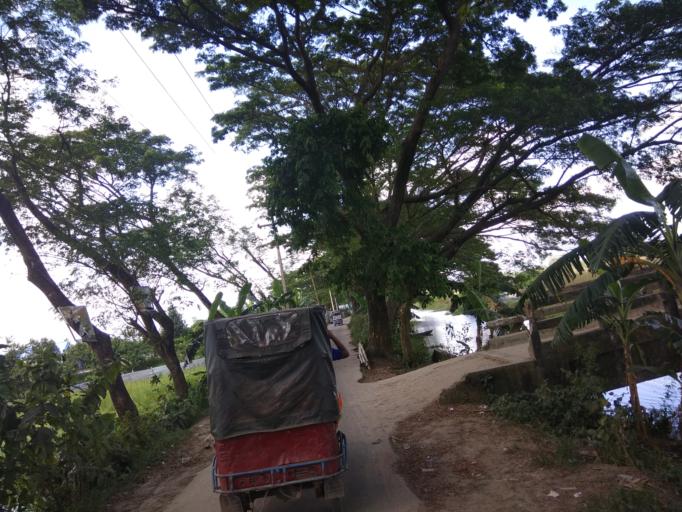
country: BD
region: Dhaka
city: Narayanganj
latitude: 23.4671
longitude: 90.4554
